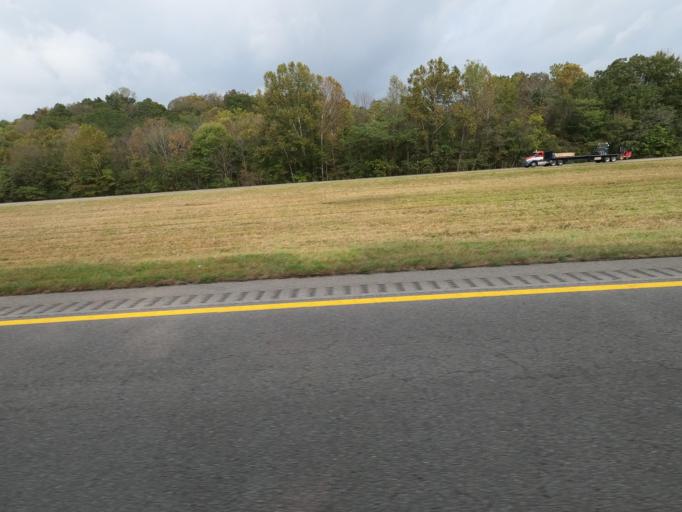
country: US
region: Tennessee
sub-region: Dickson County
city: White Bluff
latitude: 36.0243
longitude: -87.2221
